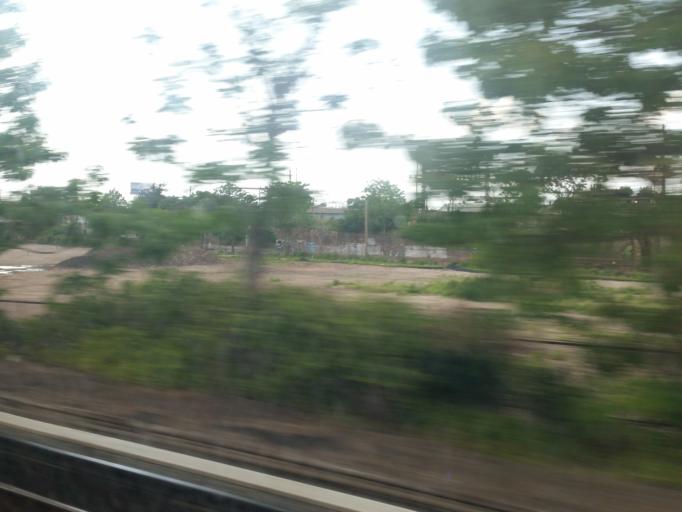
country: US
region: New Jersey
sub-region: Hudson County
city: Harrison
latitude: 40.7412
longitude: -74.1523
